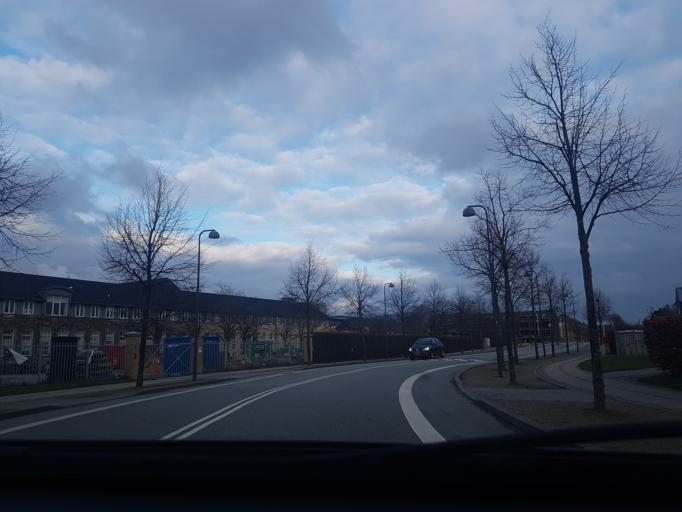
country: DK
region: Capital Region
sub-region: Kobenhavn
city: Christianshavn
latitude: 55.6779
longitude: 12.6020
